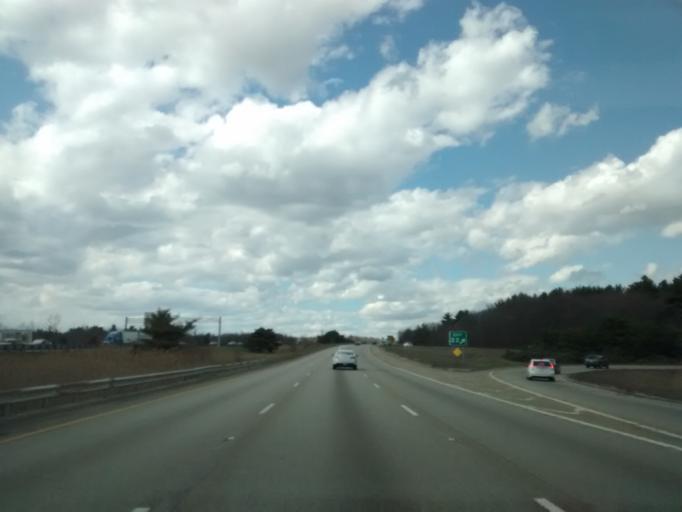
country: US
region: Massachusetts
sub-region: Worcester County
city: Cordaville
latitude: 42.2633
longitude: -71.5631
